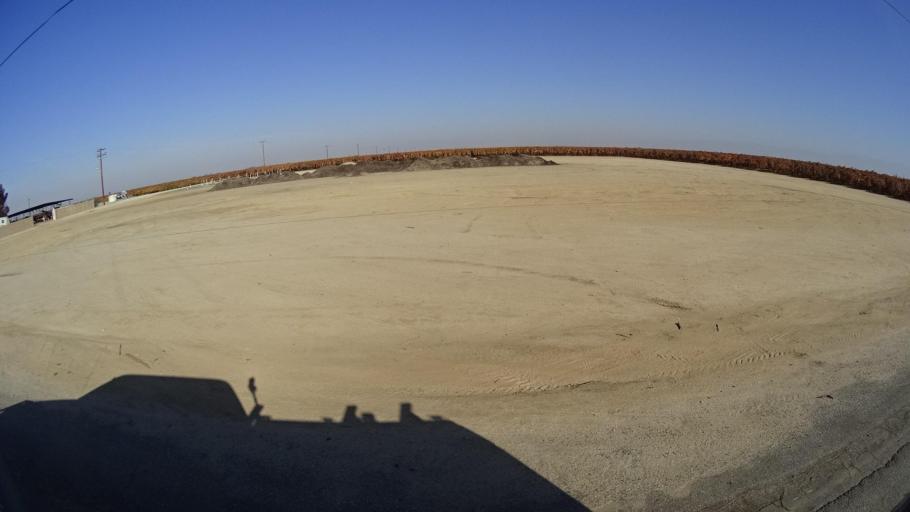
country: US
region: California
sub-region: Tulare County
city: Richgrove
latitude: 35.7471
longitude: -119.1598
